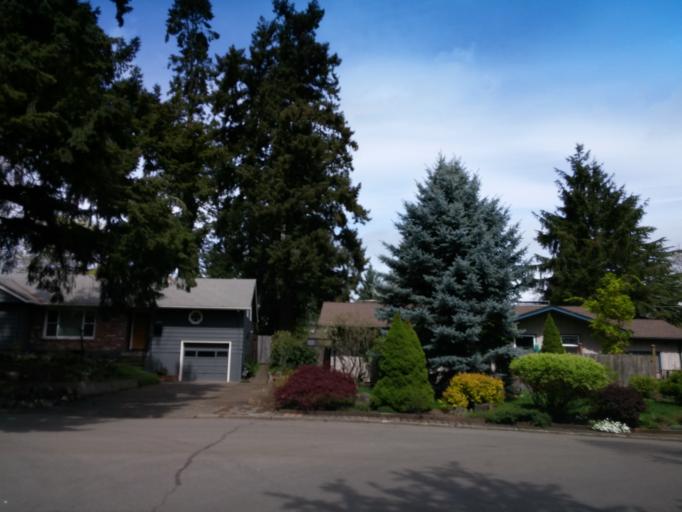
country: US
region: Oregon
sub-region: Washington County
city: Cedar Hills
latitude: 45.5049
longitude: -122.8079
